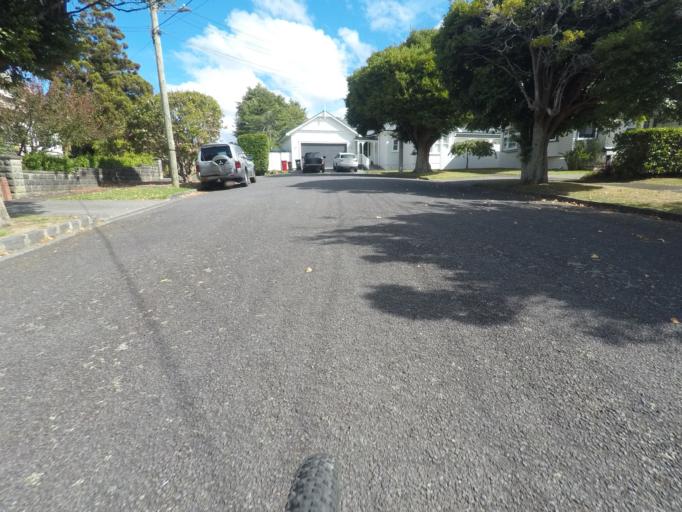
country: NZ
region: Auckland
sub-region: Auckland
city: Rosebank
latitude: -36.8813
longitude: 174.7140
